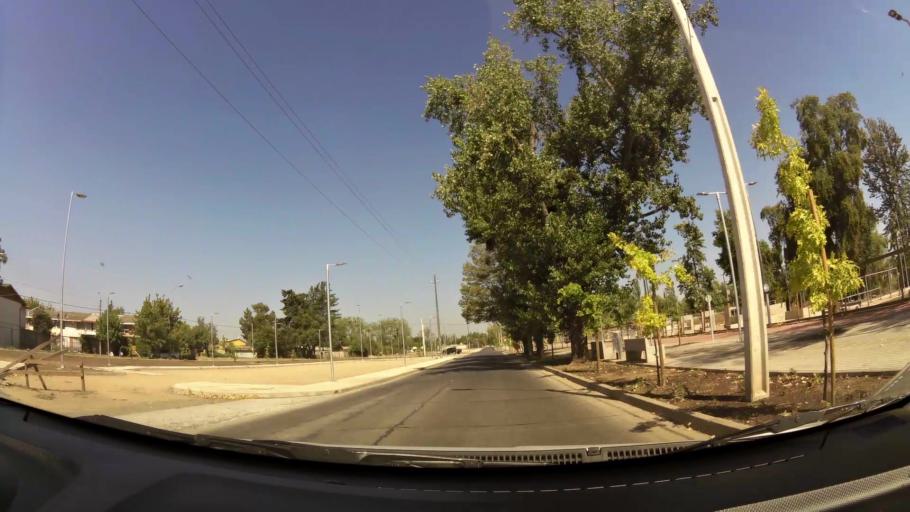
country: CL
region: Maule
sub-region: Provincia de Talca
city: Talca
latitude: -35.4370
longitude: -71.6608
